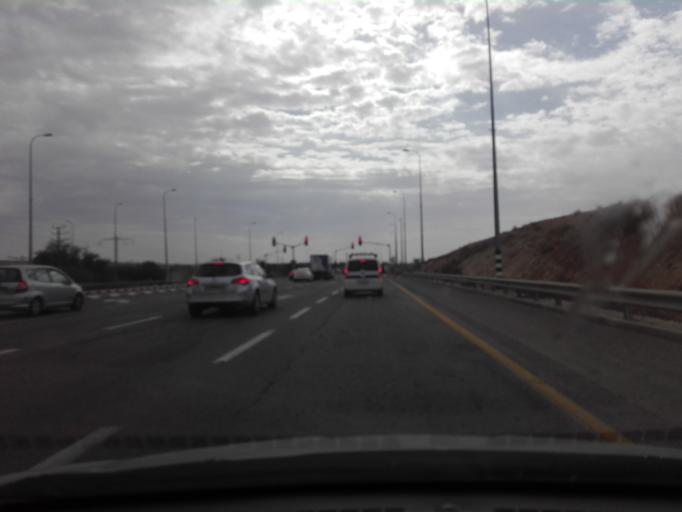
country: IL
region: Southern District
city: Beersheba
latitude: 31.3120
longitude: 34.7880
